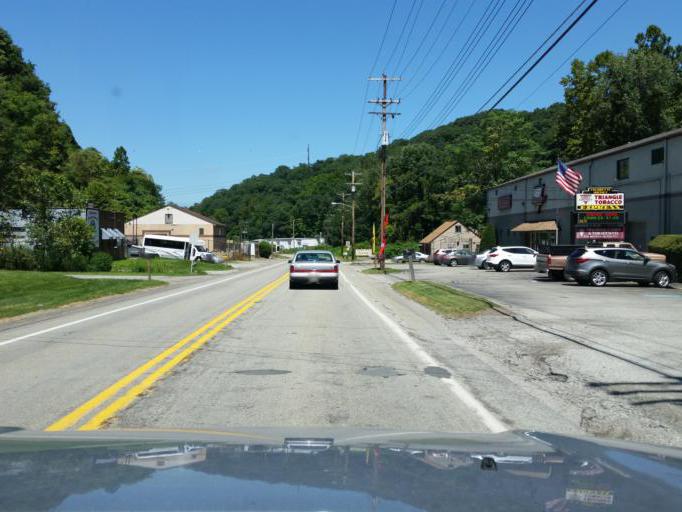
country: US
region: Pennsylvania
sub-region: Allegheny County
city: Blawnox
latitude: 40.4810
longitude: -79.8500
